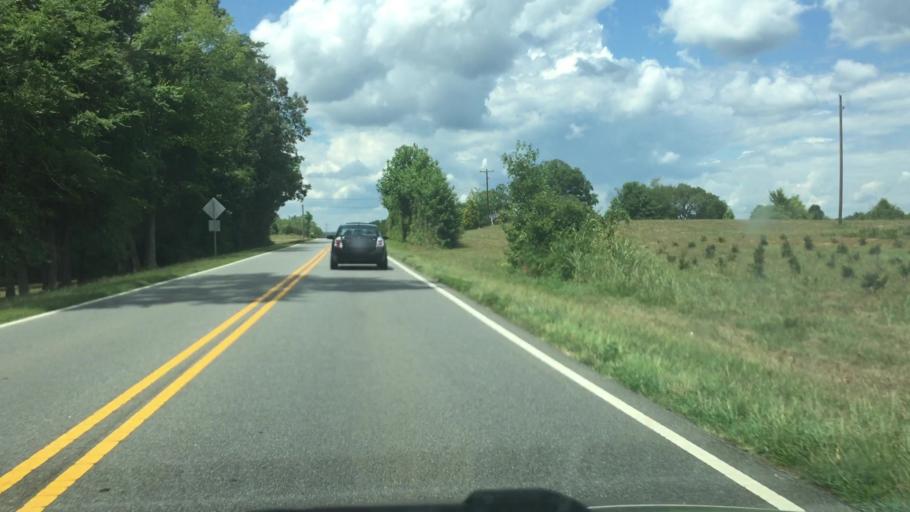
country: US
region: North Carolina
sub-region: Rowan County
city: Enochville
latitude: 35.4874
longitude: -80.6897
